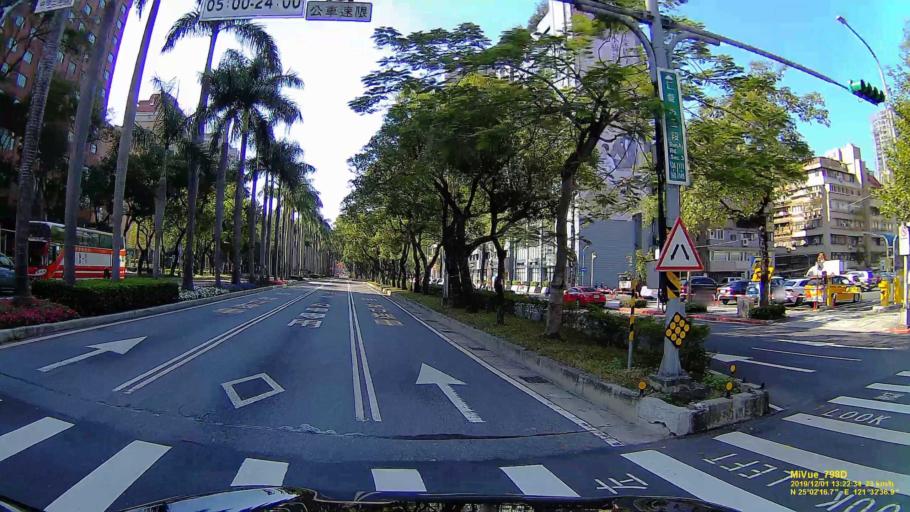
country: TW
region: Taipei
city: Taipei
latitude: 25.0380
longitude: 121.5435
